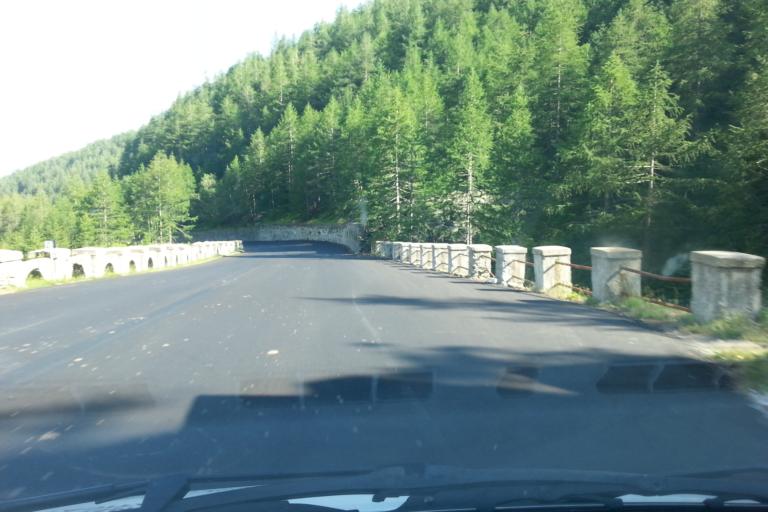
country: IT
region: Piedmont
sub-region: Provincia di Torino
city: Moncenisio
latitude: 45.2033
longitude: 6.9678
